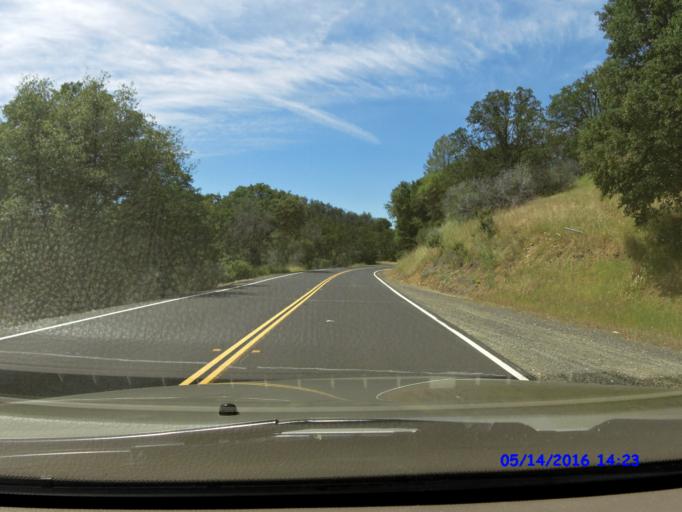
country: US
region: California
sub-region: Tuolumne County
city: Tuolumne City
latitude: 37.6898
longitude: -120.1806
